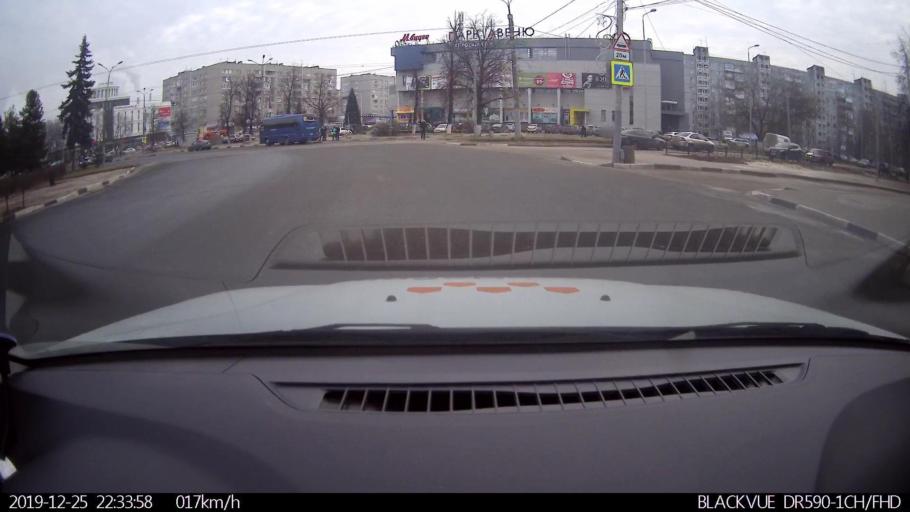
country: RU
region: Nizjnij Novgorod
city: Gorbatovka
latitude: 56.2405
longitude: 43.8631
